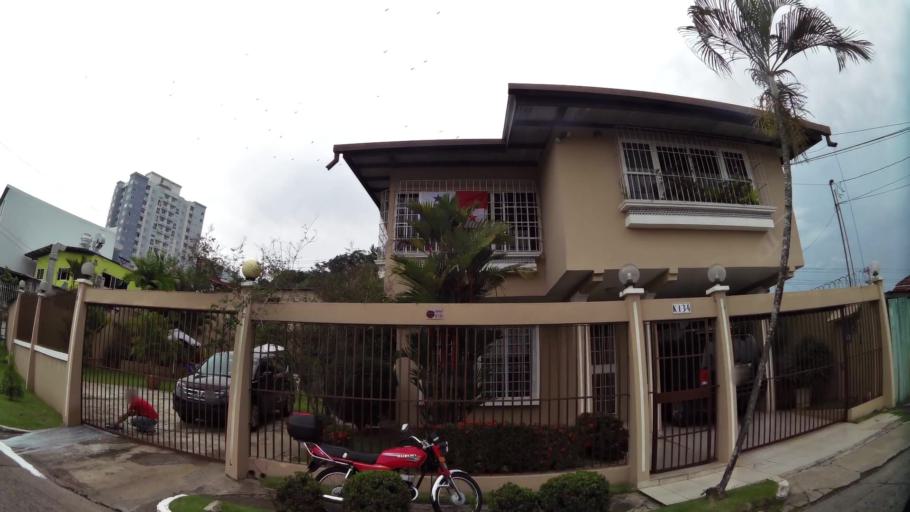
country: PA
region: Panama
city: Panama
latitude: 9.0217
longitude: -79.5277
